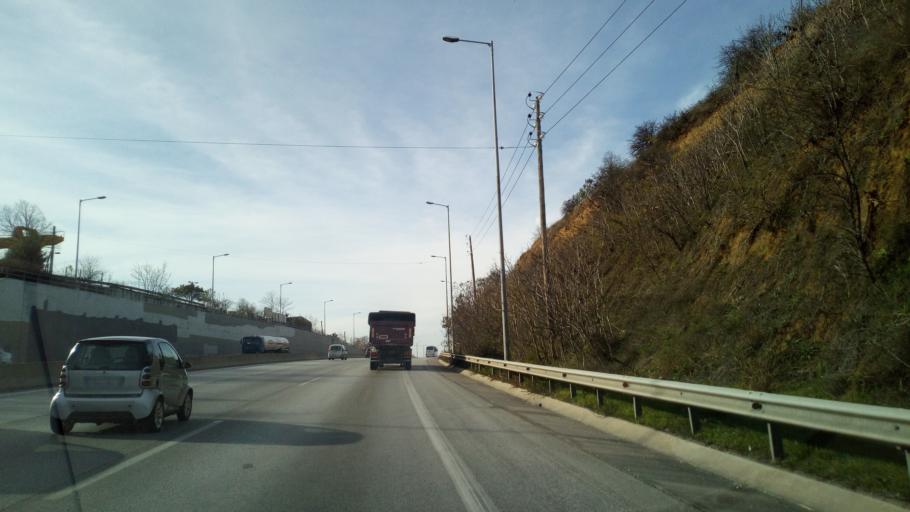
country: GR
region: Central Macedonia
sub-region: Nomos Thessalonikis
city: Liti
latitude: 40.7243
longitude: 22.9794
